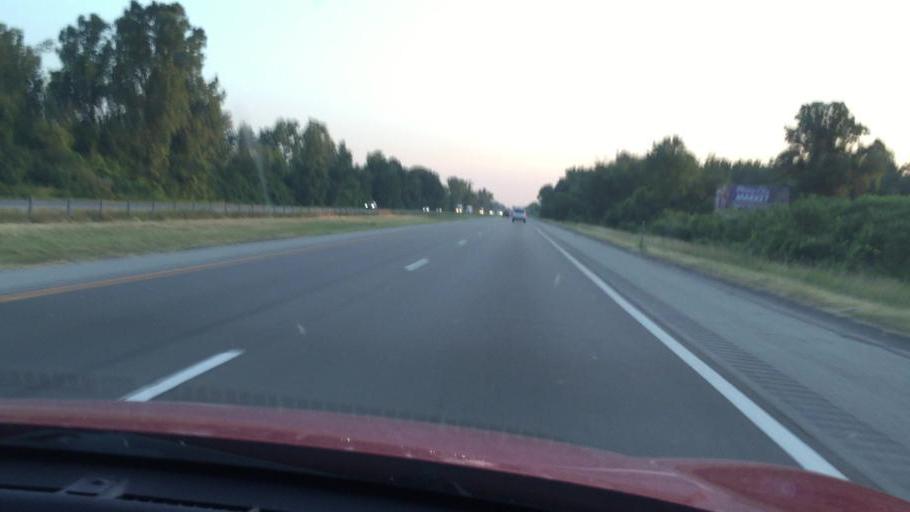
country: US
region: Michigan
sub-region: Washtenaw County
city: Milan
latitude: 42.0507
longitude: -83.6698
